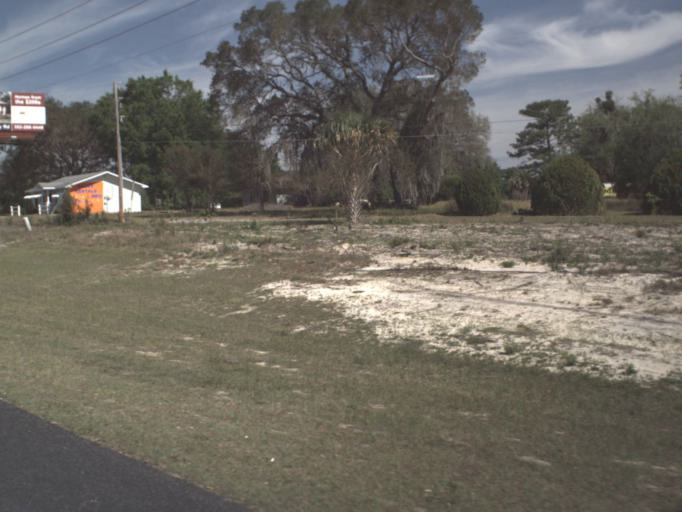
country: US
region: Florida
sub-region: Sumter County
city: The Villages
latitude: 28.9806
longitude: -81.9859
